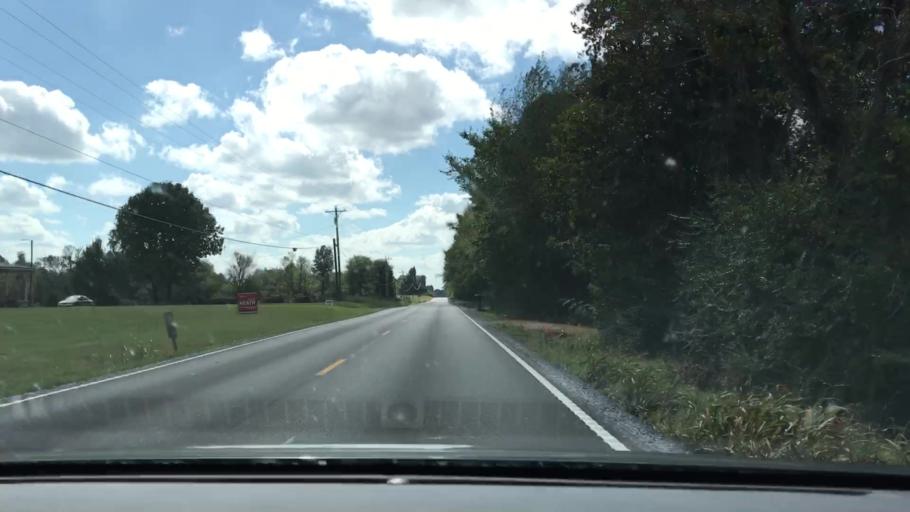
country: US
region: Kentucky
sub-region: Graves County
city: Mayfield
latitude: 36.7997
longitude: -88.5954
